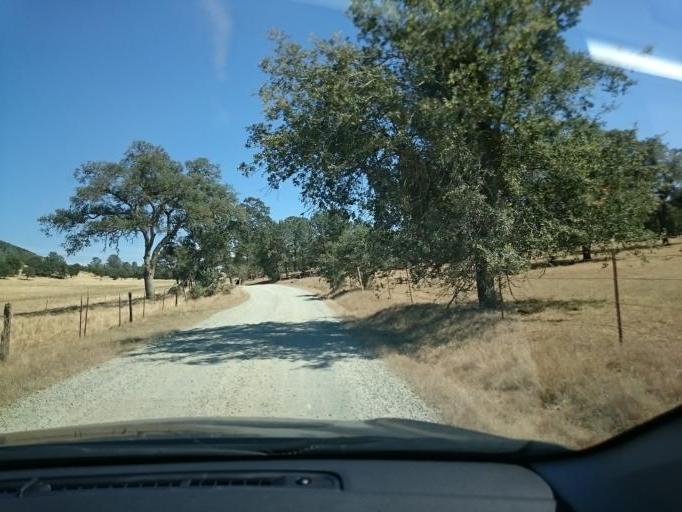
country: US
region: California
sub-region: Calaveras County
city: Rancho Calaveras
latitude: 38.1012
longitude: -120.7653
